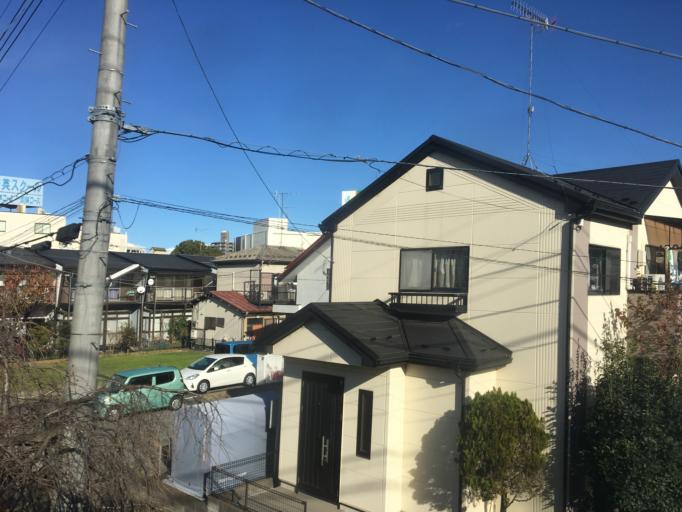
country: JP
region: Saitama
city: Fukiage-fujimi
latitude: 36.0376
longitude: 139.4003
